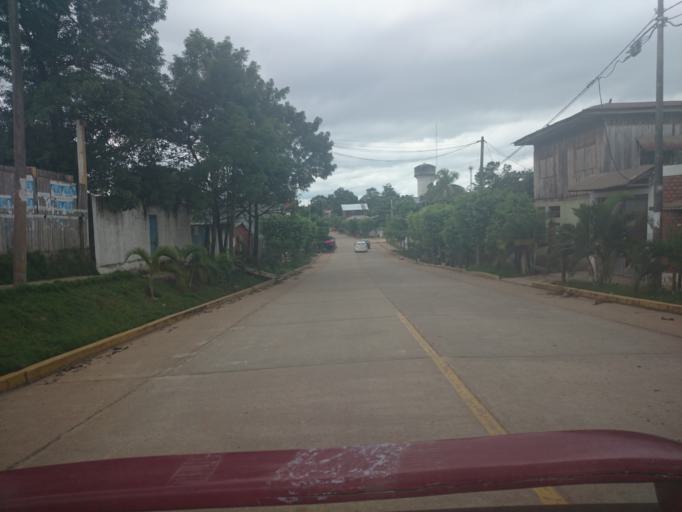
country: PE
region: Ucayali
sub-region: Provincia de Coronel Portillo
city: Puerto Callao
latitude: -8.3592
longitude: -74.5751
